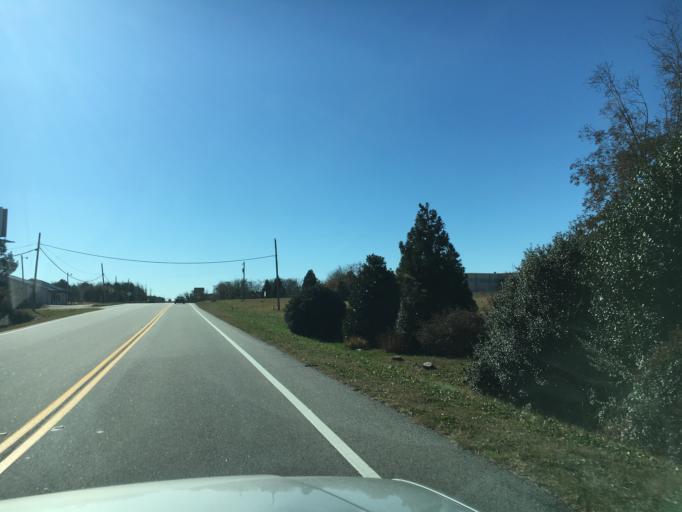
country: US
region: Georgia
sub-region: Hart County
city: Hartwell
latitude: 34.3381
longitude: -82.9571
